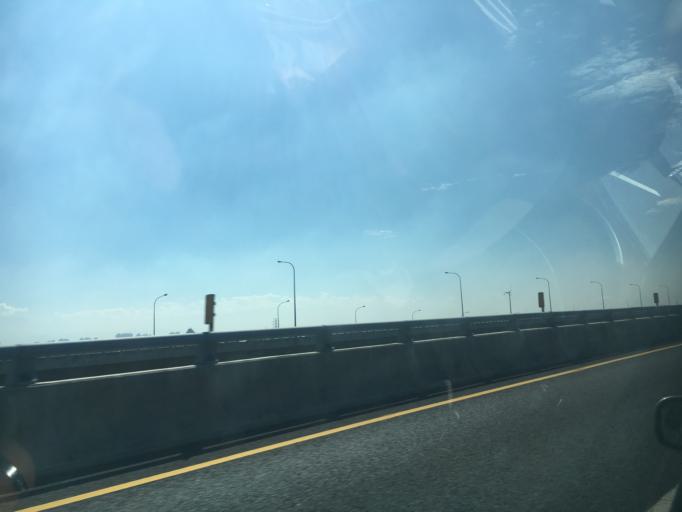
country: TW
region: Taiwan
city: Taoyuan City
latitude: 25.0232
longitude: 121.2781
